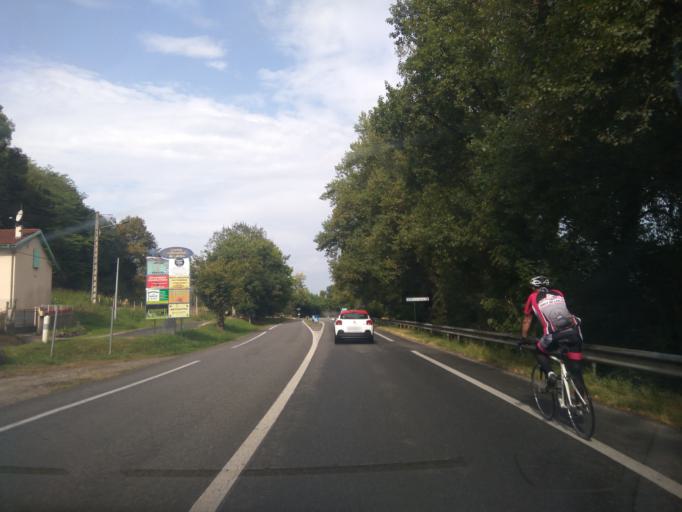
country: FR
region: Aquitaine
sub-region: Departement des Pyrenees-Atlantiques
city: Artiguelouve
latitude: 43.3040
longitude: -0.4364
